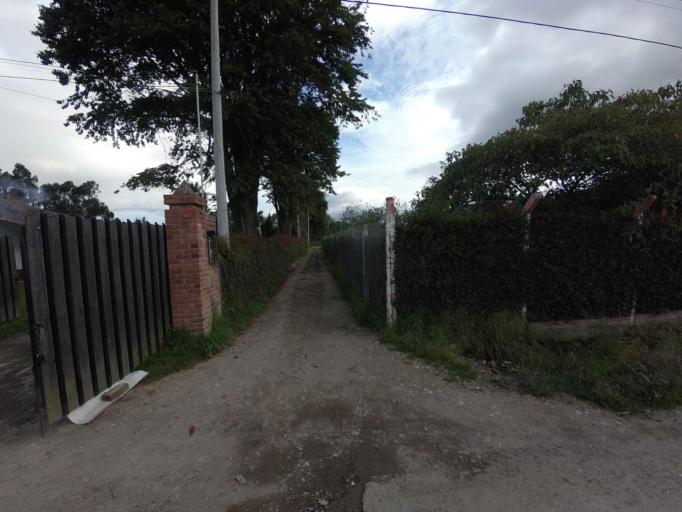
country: CO
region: Cundinamarca
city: Tabio
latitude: 4.9247
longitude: -74.0866
